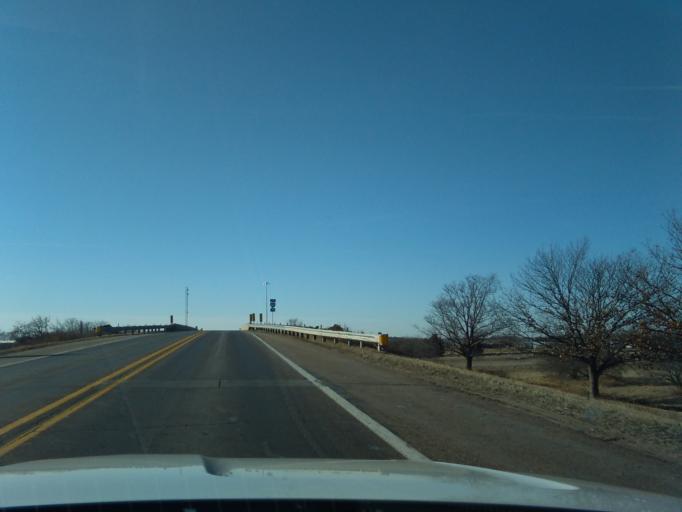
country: US
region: Nebraska
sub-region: Seward County
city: Milford
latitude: 40.8233
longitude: -97.1019
